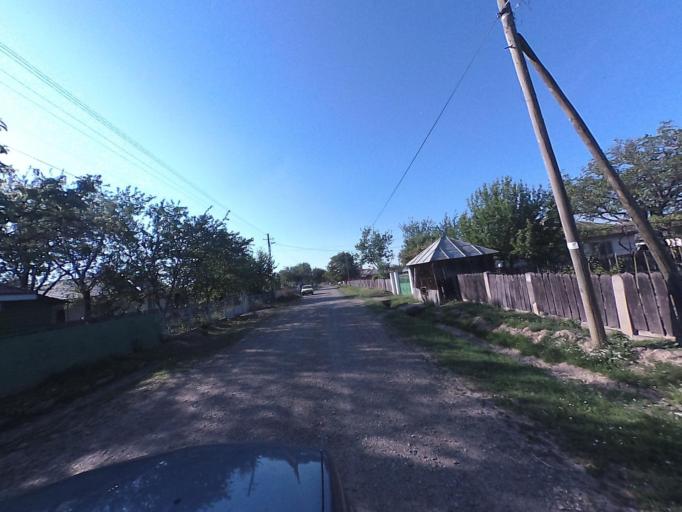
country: RO
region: Neamt
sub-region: Comuna Cordun
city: Pildesti
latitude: 46.9828
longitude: 26.8076
